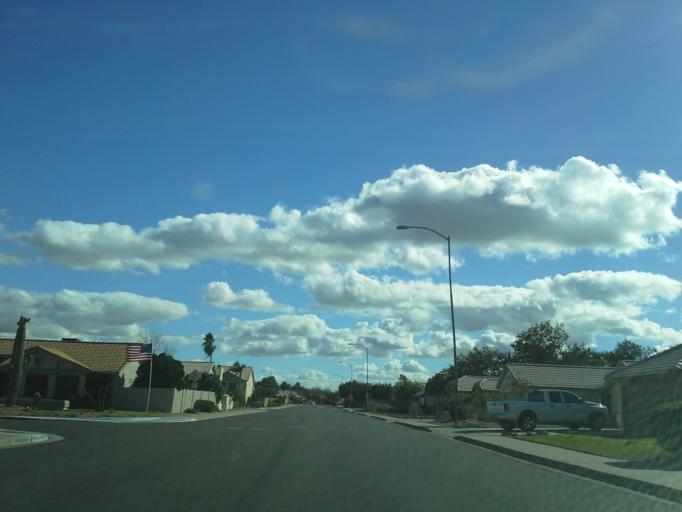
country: US
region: Arizona
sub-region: Maricopa County
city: Gilbert
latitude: 33.3978
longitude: -111.7154
